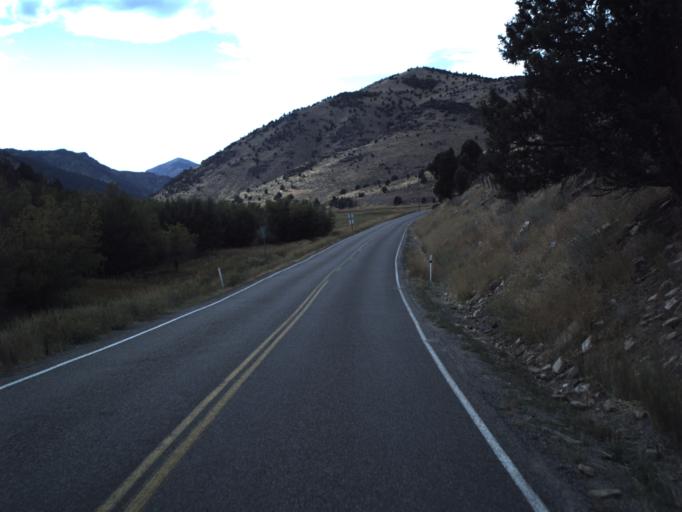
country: US
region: Utah
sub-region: Cache County
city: Millville
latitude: 41.6021
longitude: -111.5730
